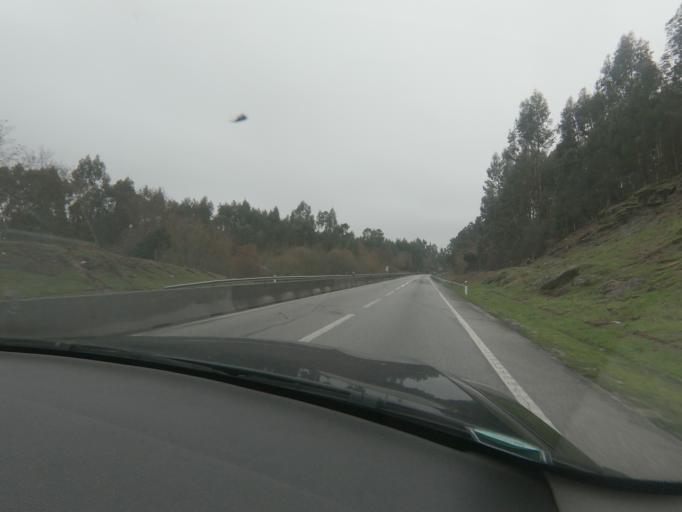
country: PT
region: Viseu
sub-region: Viseu
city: Viseu
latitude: 40.5991
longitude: -7.9964
